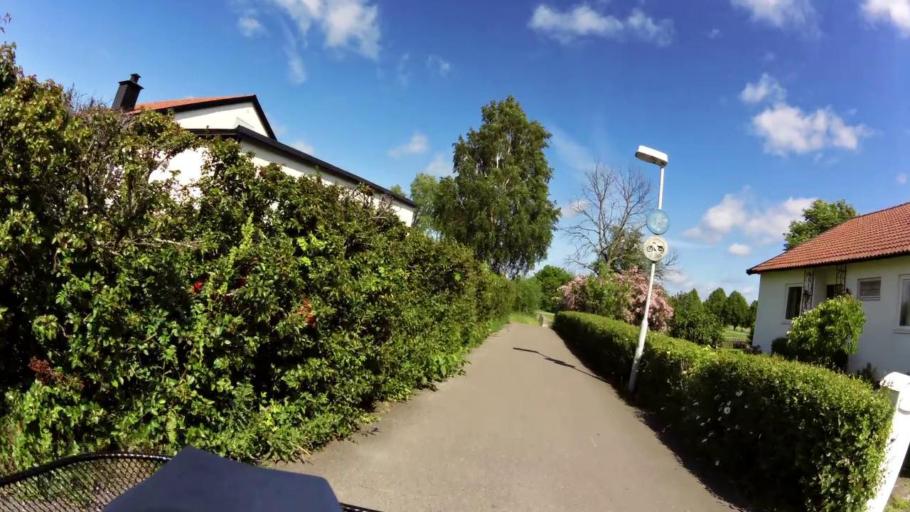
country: SE
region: OEstergoetland
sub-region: Linkopings Kommun
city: Linkoping
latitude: 58.3831
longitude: 15.6447
